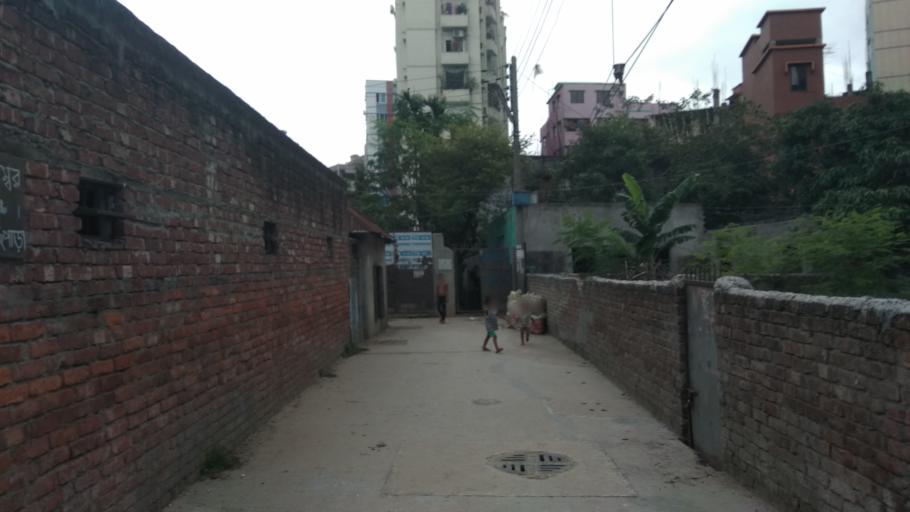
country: BD
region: Dhaka
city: Azimpur
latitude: 23.8006
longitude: 90.3756
